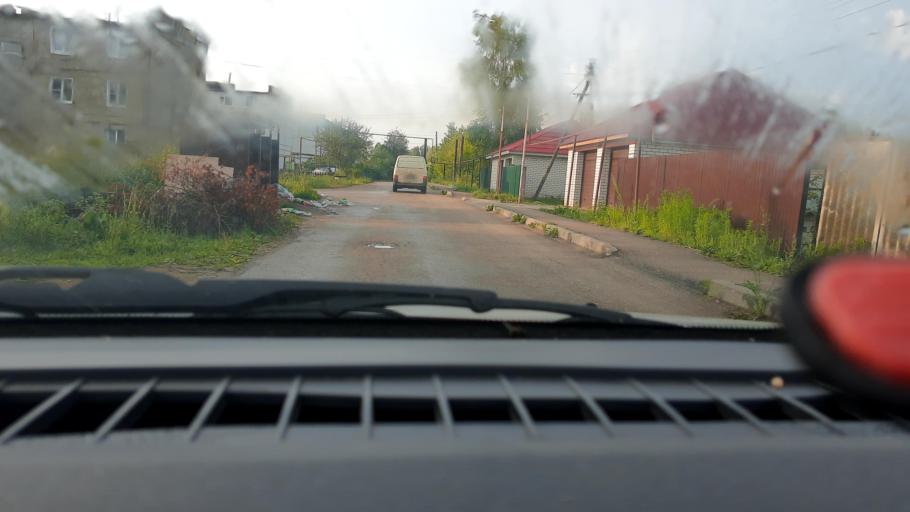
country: RU
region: Nizjnij Novgorod
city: Lukoyanov
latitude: 55.0431
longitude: 44.4941
